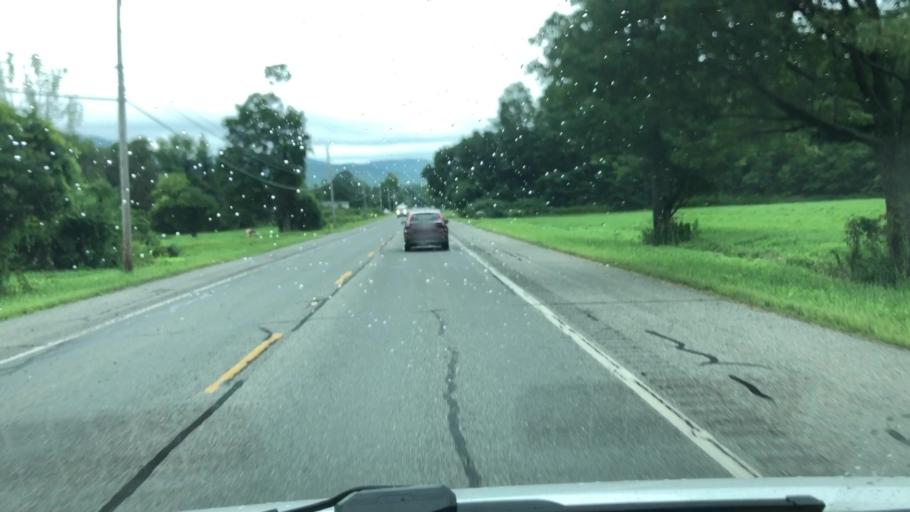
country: US
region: Massachusetts
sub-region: Berkshire County
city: Williamstown
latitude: 42.6479
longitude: -73.2362
